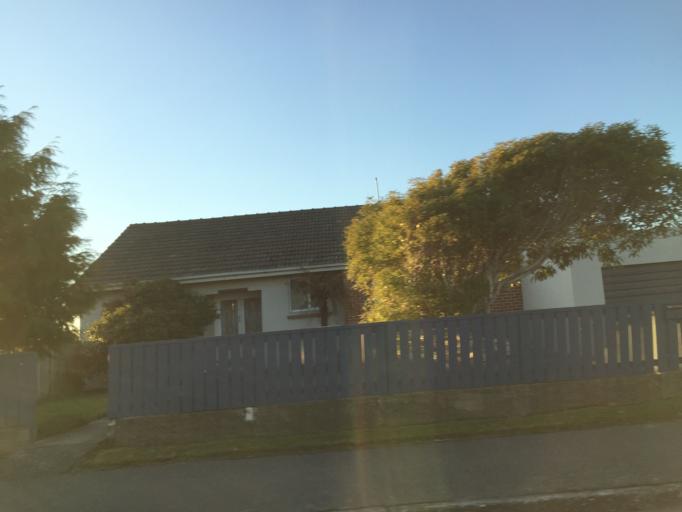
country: NZ
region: Southland
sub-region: Invercargill City
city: Invercargill
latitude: -46.4178
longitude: 168.3804
